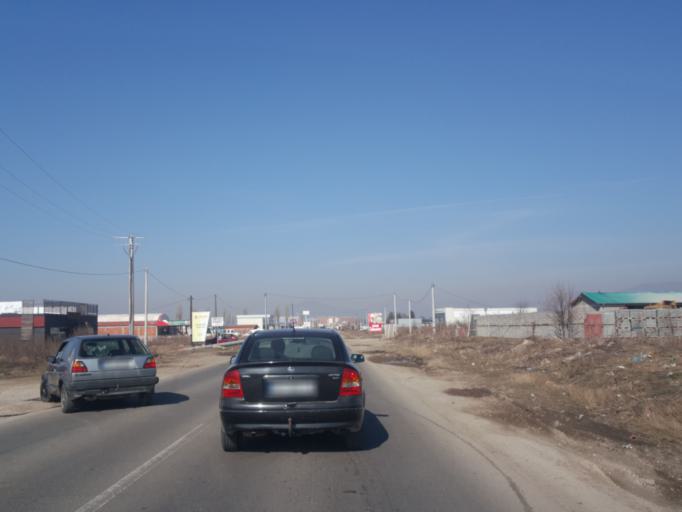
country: XK
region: Mitrovica
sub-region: Vushtrri
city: Vushtrri
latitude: 42.8057
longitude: 20.9908
